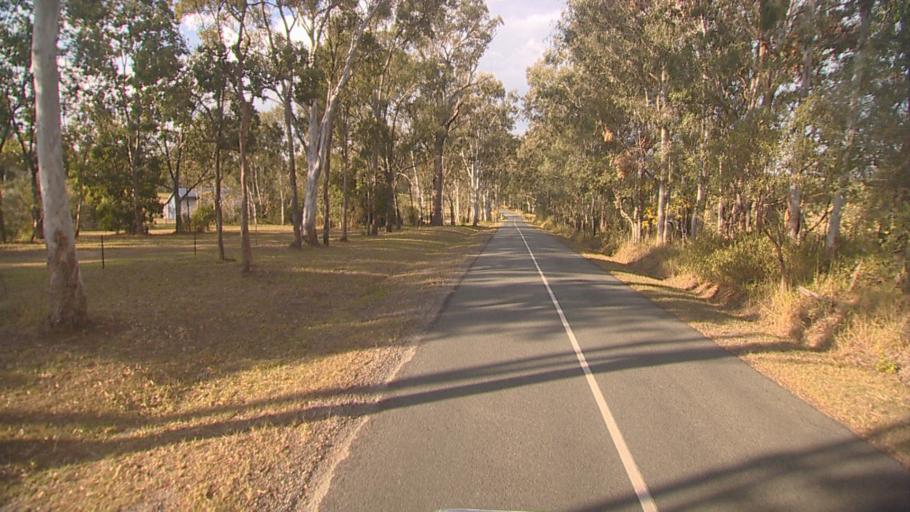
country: AU
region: Queensland
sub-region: Logan
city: Cedar Vale
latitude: -27.8500
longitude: 153.1355
